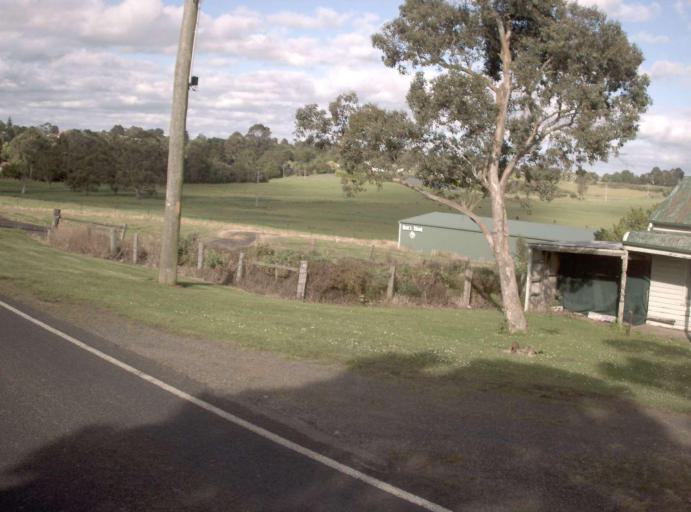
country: AU
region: Victoria
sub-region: Baw Baw
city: Warragul
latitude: -38.4854
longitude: 145.9368
